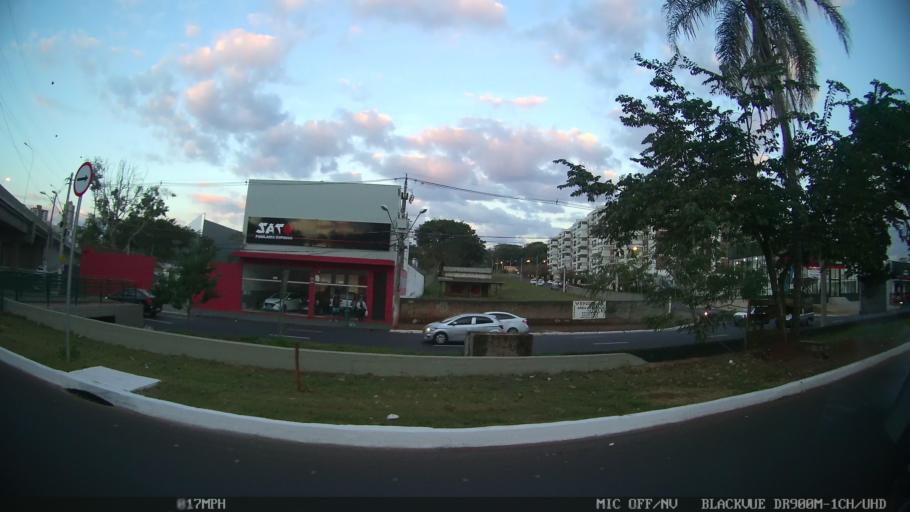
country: BR
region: Sao Paulo
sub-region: Ribeirao Preto
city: Ribeirao Preto
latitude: -21.1925
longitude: -47.7979
